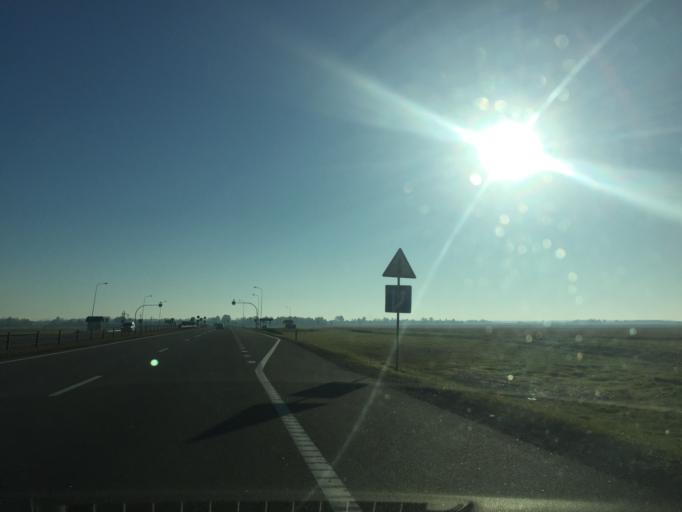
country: BY
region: Minsk
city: Smilavichy
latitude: 53.7592
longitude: 27.9556
